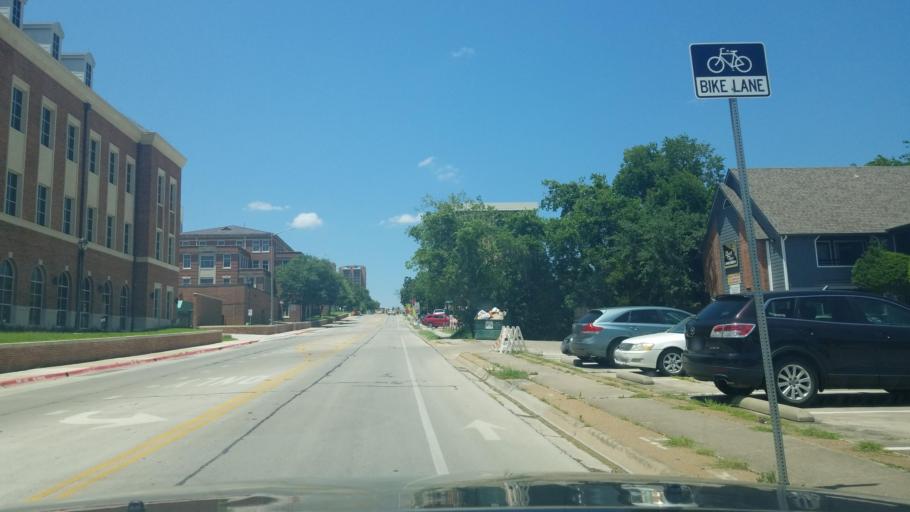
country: US
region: Texas
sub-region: Denton County
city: Denton
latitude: 33.2224
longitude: -97.1273
